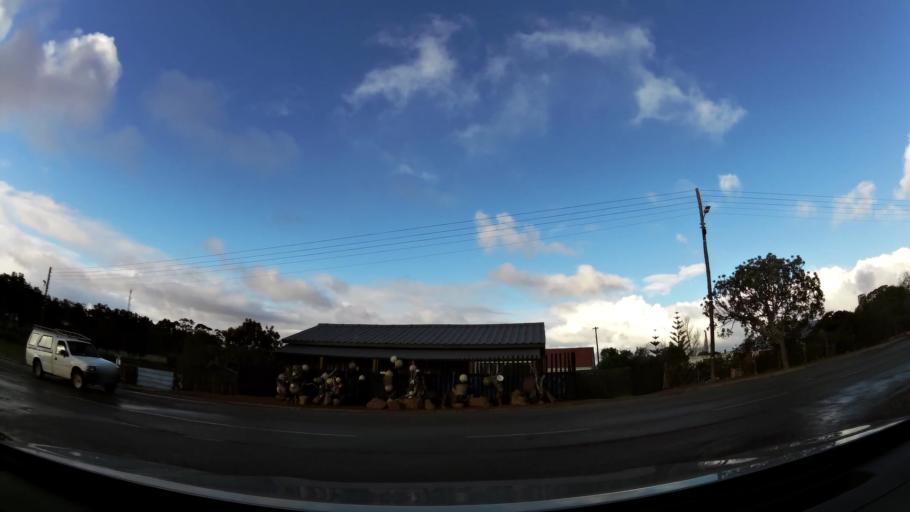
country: ZA
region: Western Cape
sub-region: Eden District Municipality
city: Riversdale
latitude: -34.2019
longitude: 21.5850
